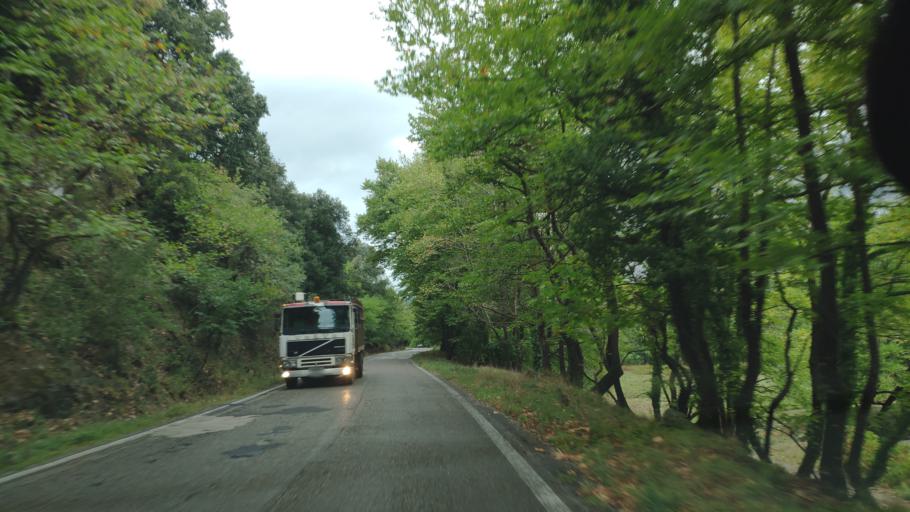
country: GR
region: West Greece
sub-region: Nomos Aitolias kai Akarnanias
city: Krikellos
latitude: 38.9550
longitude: 21.3388
